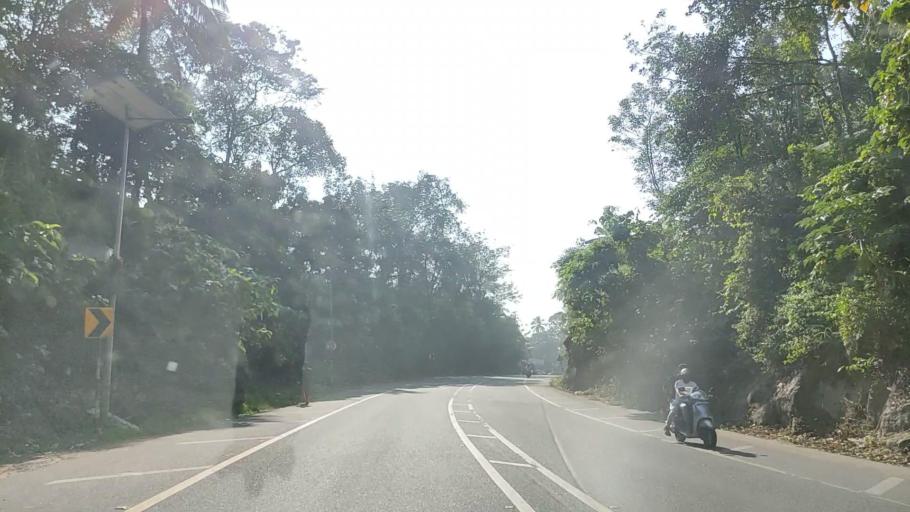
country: IN
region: Kerala
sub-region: Kollam
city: Punalur
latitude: 8.8912
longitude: 76.8664
